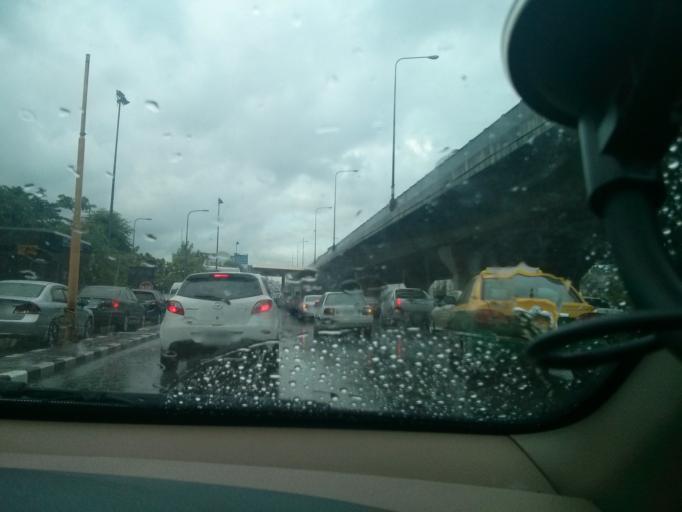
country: TH
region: Nonthaburi
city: Mueang Nonthaburi
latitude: 13.8531
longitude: 100.5335
